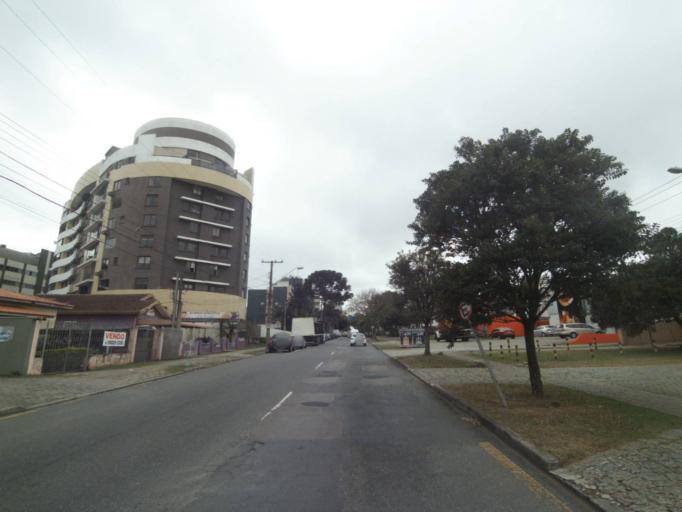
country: BR
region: Parana
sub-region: Curitiba
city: Curitiba
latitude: -25.4509
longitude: -49.2972
